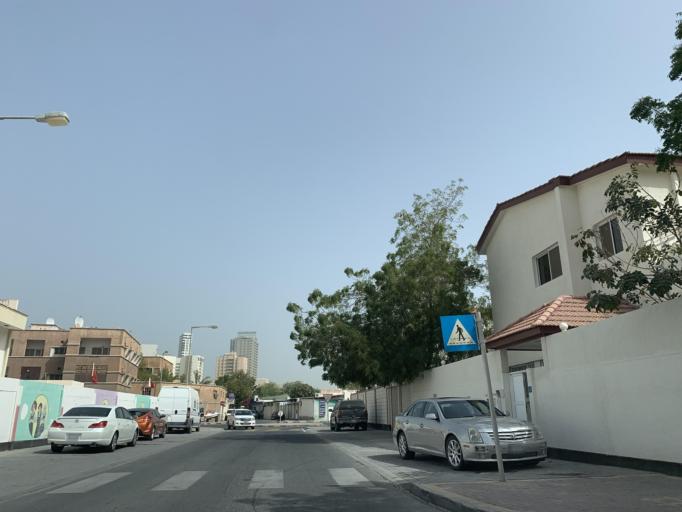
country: BH
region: Manama
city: Manama
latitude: 26.2075
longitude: 50.6007
